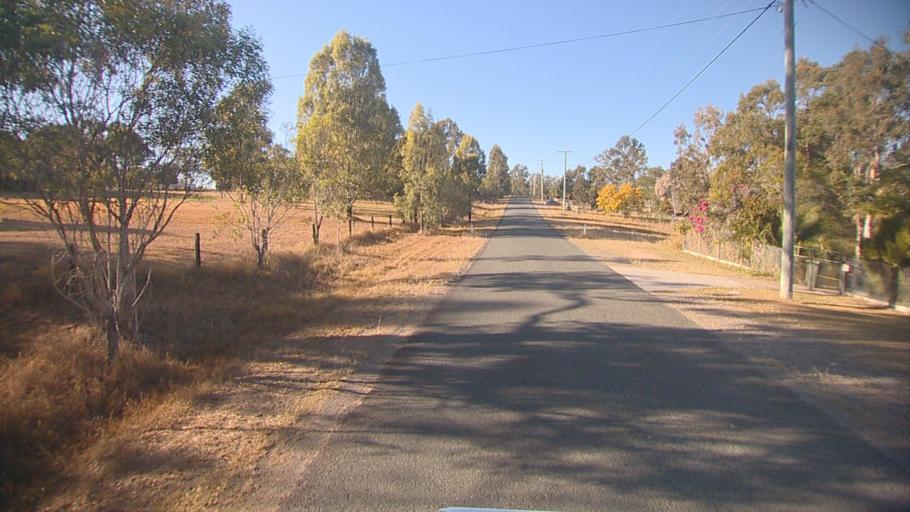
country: AU
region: Queensland
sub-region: Logan
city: Cedar Vale
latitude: -27.8344
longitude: 153.0066
